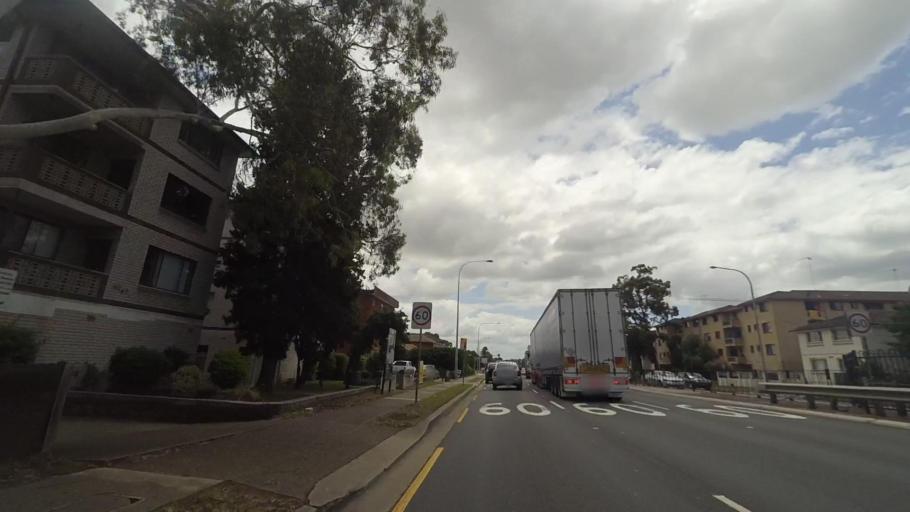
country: AU
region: New South Wales
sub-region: Fairfield
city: Liverpool
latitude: -33.9210
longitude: 150.9190
